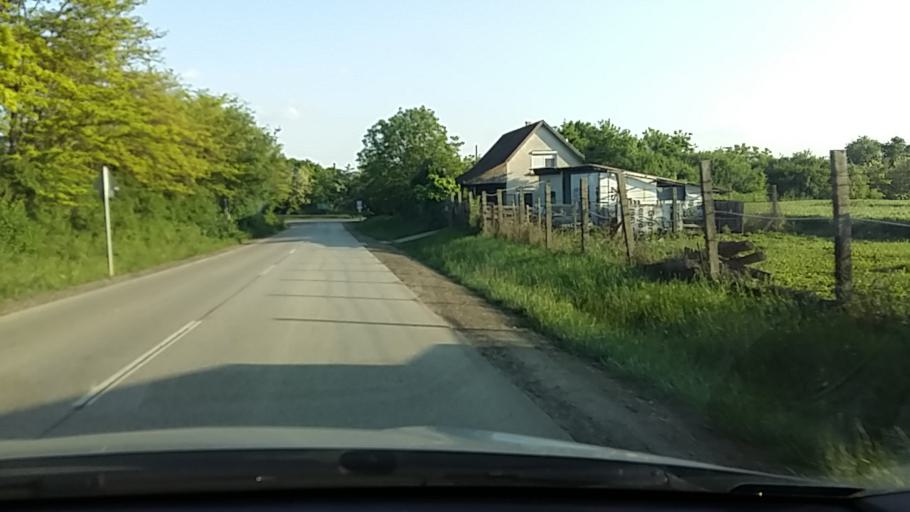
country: HU
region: Pest
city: Szod
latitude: 47.7336
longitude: 19.2219
